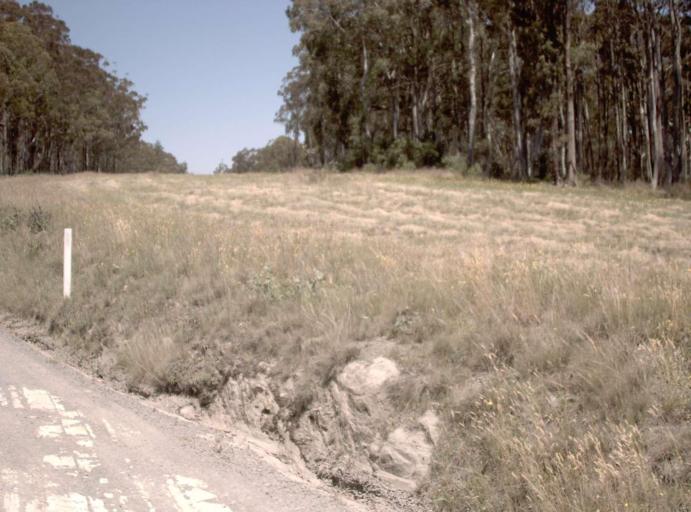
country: AU
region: Victoria
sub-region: Mansfield
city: Mansfield
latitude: -37.5947
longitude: 146.2021
